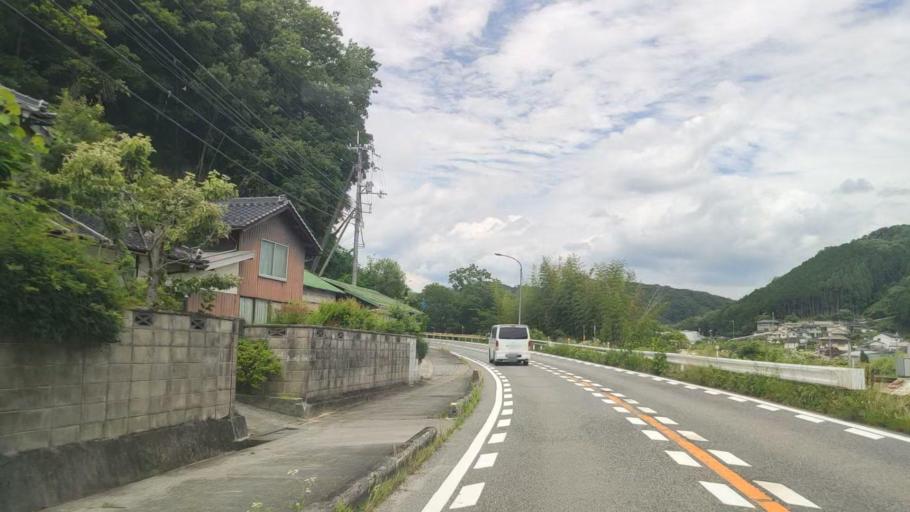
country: JP
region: Hyogo
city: Yamazakicho-nakabirose
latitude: 34.9832
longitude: 134.4259
